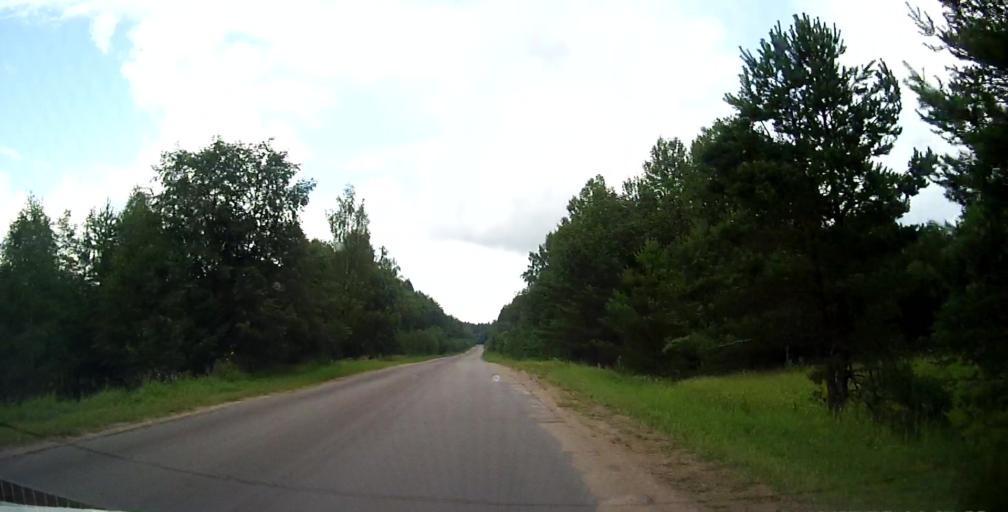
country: RU
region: Smolensk
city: Demidov
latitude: 55.4718
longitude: 31.6253
